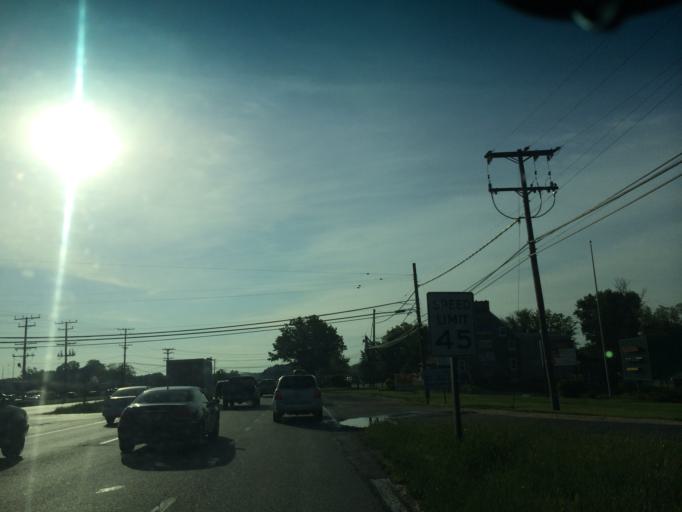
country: US
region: Maryland
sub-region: Howard County
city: Columbia
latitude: 39.2802
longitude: -76.8685
